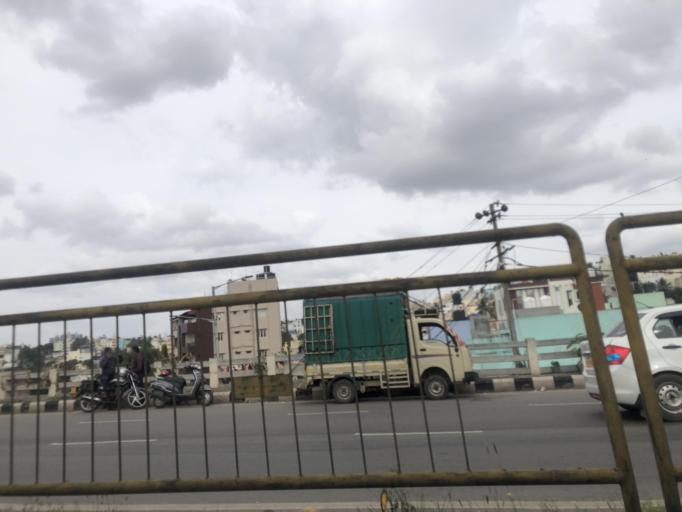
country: IN
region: Karnataka
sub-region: Bangalore Urban
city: Bangalore
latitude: 12.9979
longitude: 77.5237
